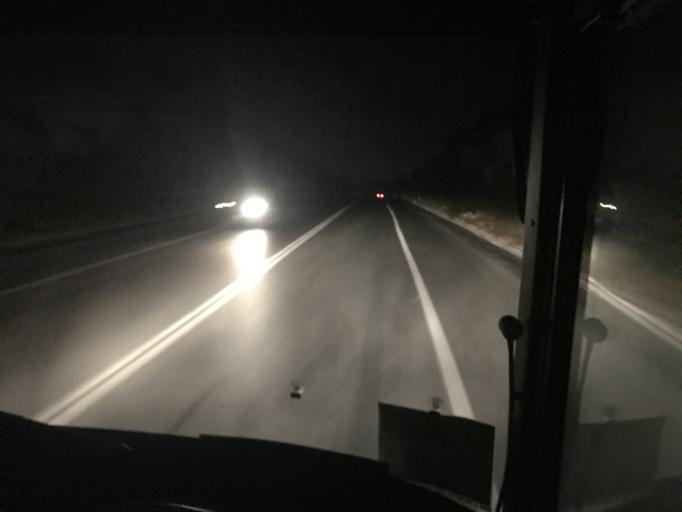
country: GR
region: Crete
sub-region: Nomos Irakleiou
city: Skalanion
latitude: 35.2772
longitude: 25.1820
